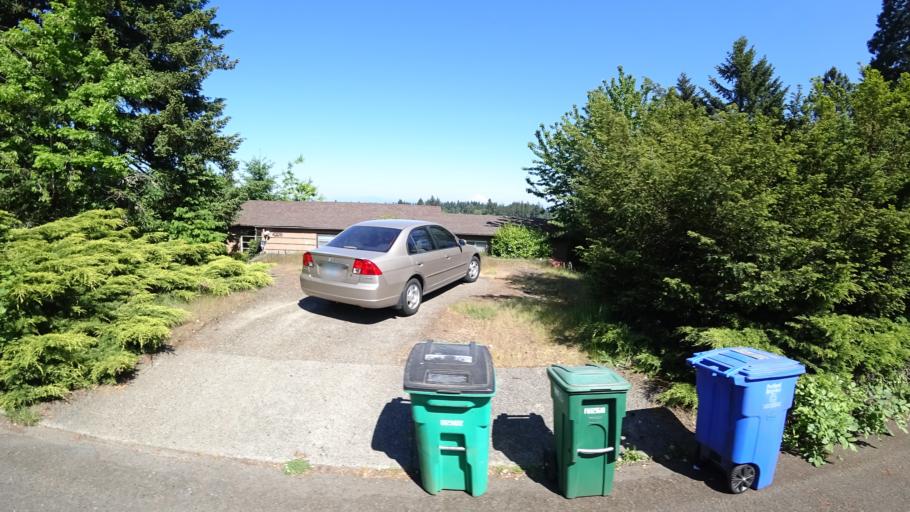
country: US
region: Oregon
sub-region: Washington County
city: Metzger
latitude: 45.4508
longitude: -122.7205
